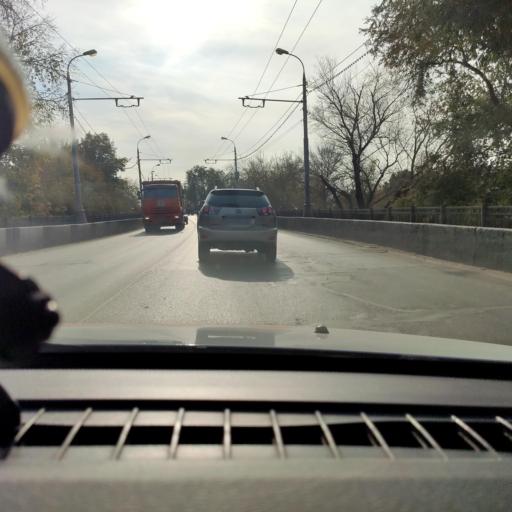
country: RU
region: Samara
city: Rozhdestveno
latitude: 53.1763
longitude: 50.0738
